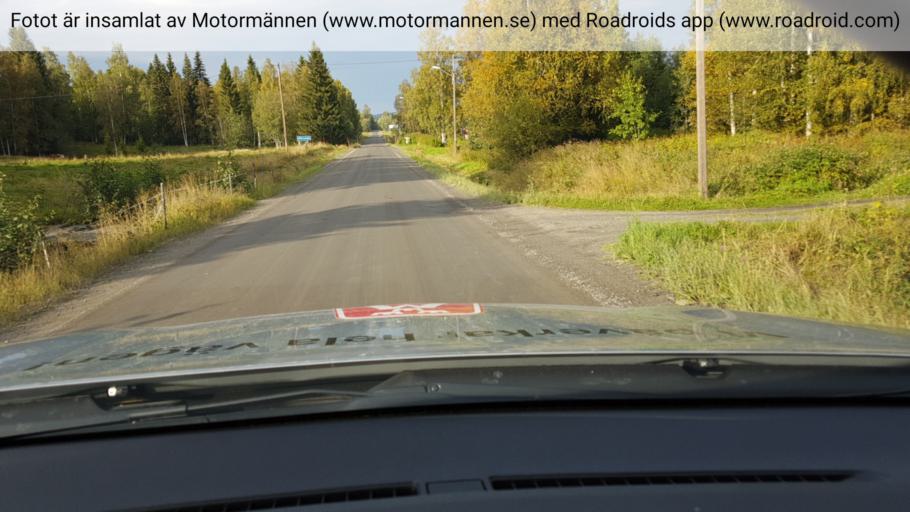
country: SE
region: Jaemtland
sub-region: Stroemsunds Kommun
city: Stroemsund
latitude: 64.0332
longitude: 15.8095
